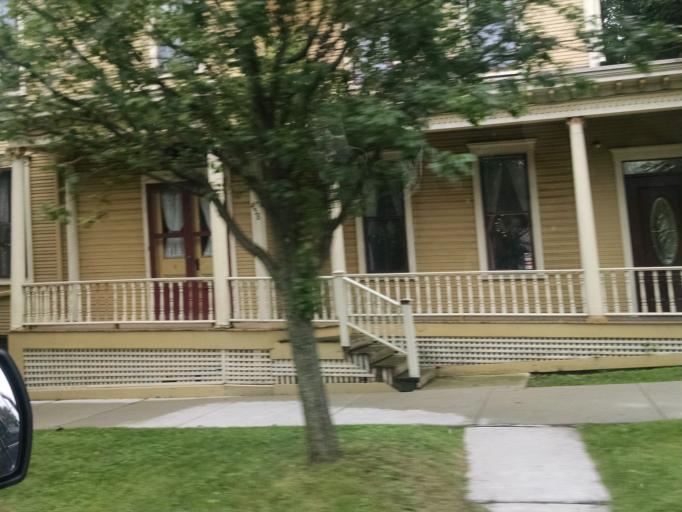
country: US
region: Pennsylvania
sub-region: Indiana County
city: Indiana
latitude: 40.6229
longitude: -79.1477
